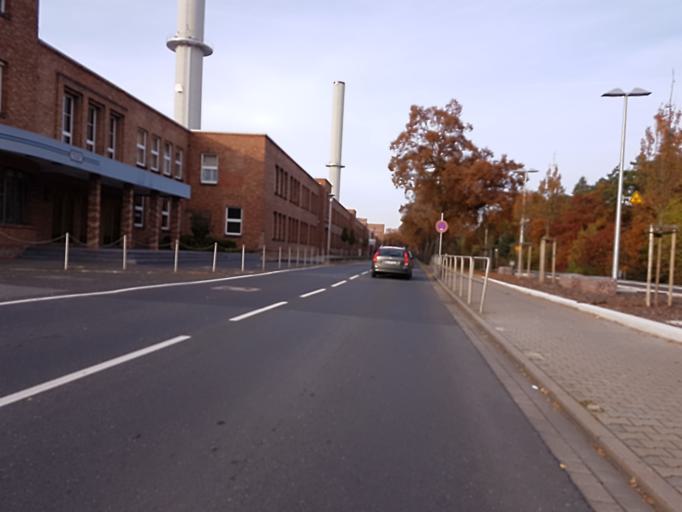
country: DE
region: Bavaria
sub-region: Regierungsbezirk Unterfranken
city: Elsenfeld
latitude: 49.8286
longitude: 9.1522
